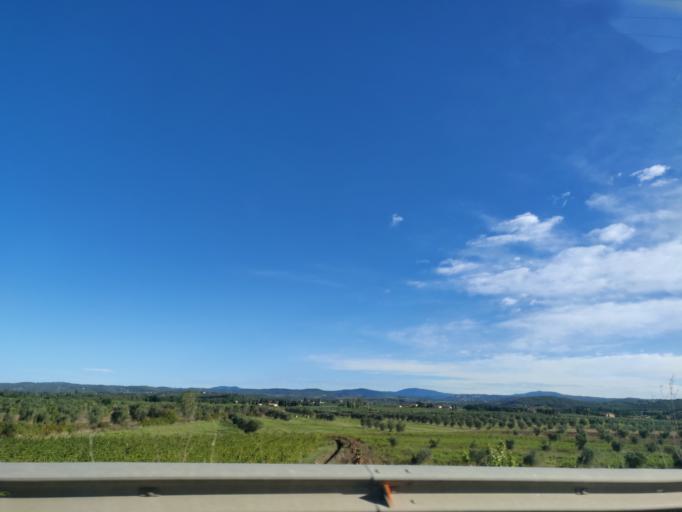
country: IT
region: Tuscany
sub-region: Provincia di Grosseto
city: Scarlino Scalo
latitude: 42.9597
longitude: 10.8095
